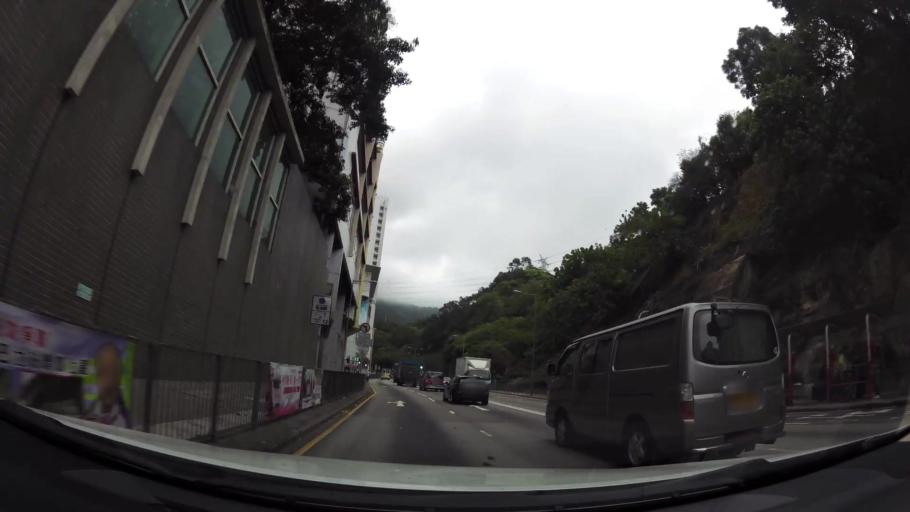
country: HK
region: Tsuen Wan
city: Tsuen Wan
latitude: 22.3773
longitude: 114.1368
